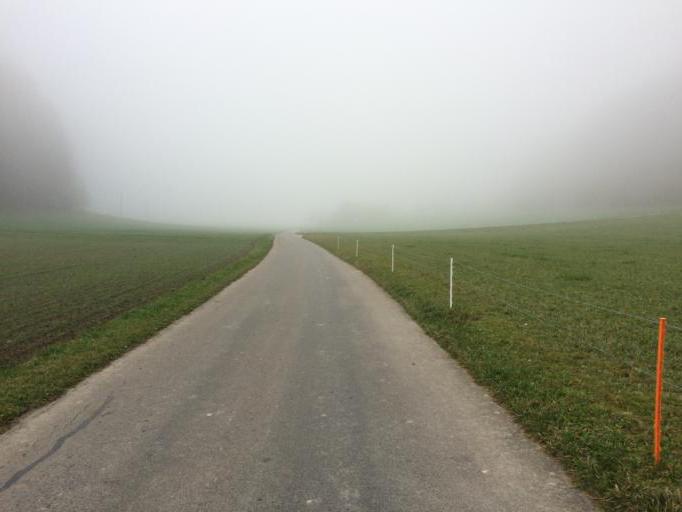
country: CH
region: Bern
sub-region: Bern-Mittelland District
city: Kehrsatz
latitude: 46.9079
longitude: 7.4545
